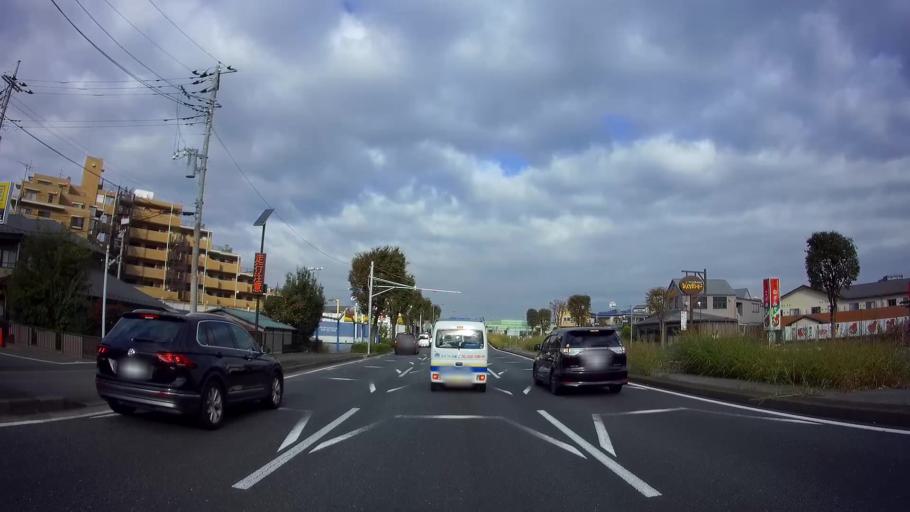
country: JP
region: Saitama
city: Yono
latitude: 35.8979
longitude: 139.6029
